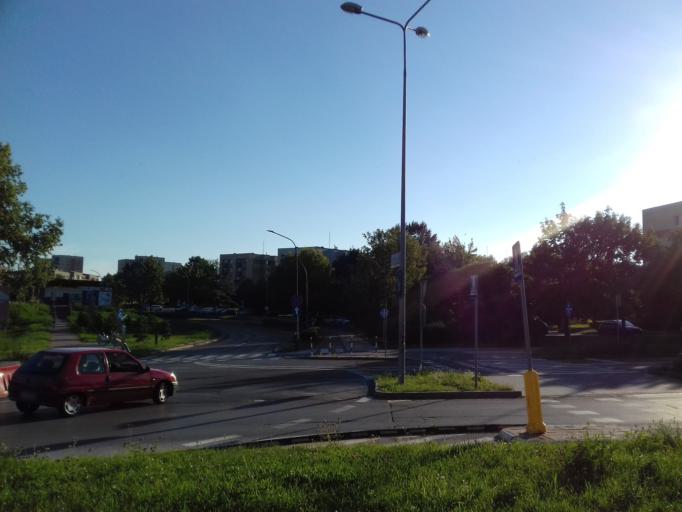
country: PL
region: Silesian Voivodeship
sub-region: Czestochowa
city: Czestochowa
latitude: 50.8414
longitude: 19.1312
